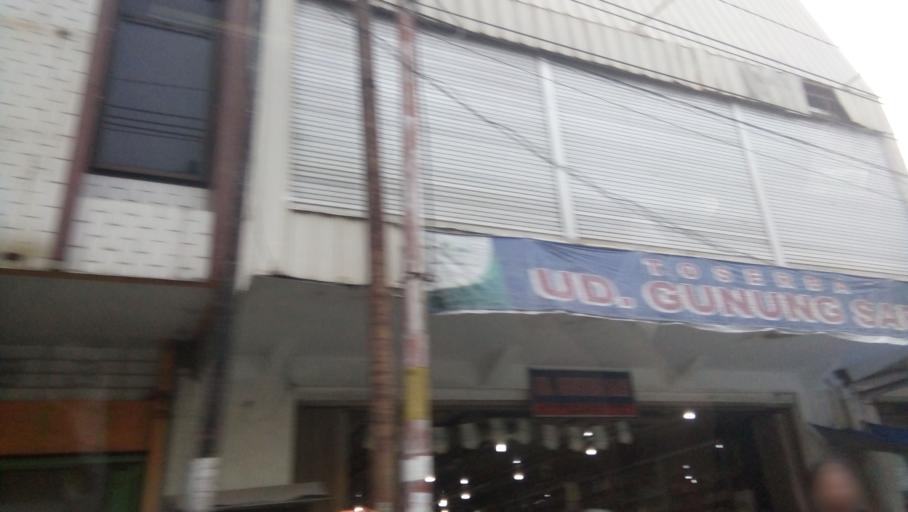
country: ID
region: Central Java
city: Surakarta
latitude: -7.5747
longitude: 110.8249
